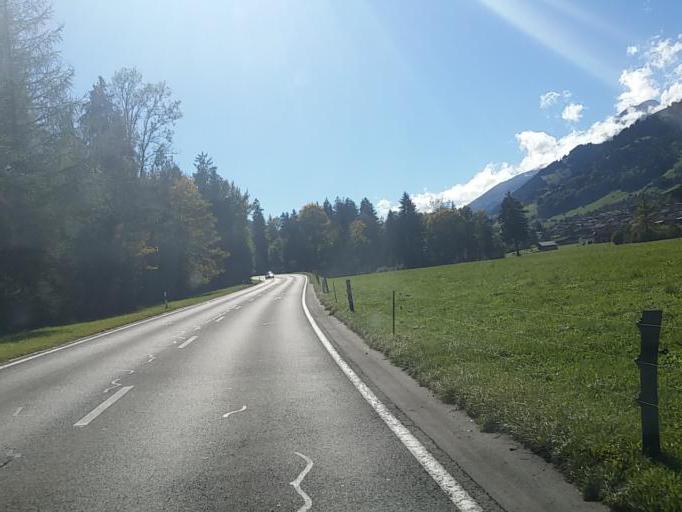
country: CH
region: Bern
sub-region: Frutigen-Niedersimmental District
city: Frutigen
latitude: 46.5988
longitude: 7.6603
